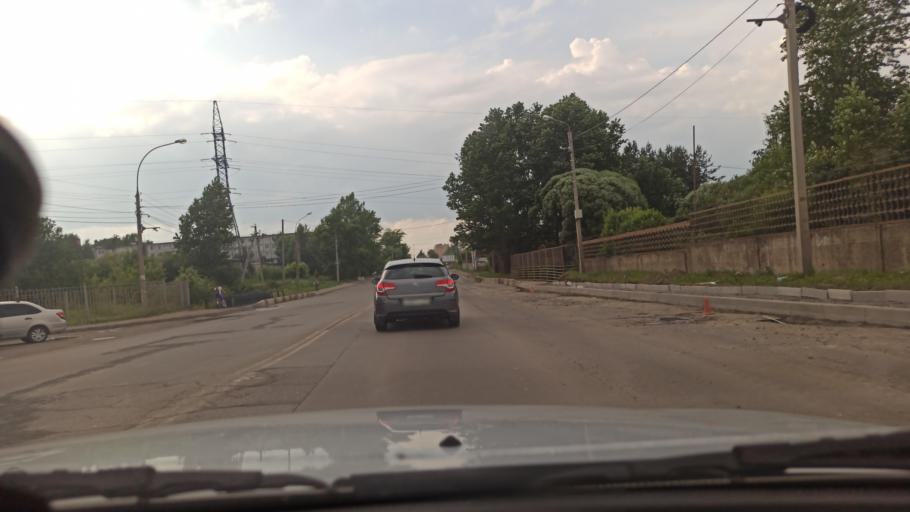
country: RU
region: Vologda
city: Vologda
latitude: 59.2026
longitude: 39.8548
